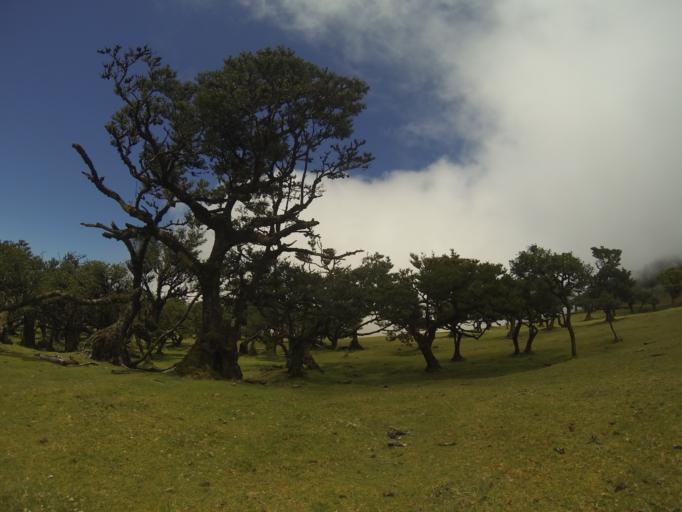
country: PT
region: Madeira
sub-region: Porto Moniz
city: Porto Moniz
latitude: 32.8113
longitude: -17.1442
